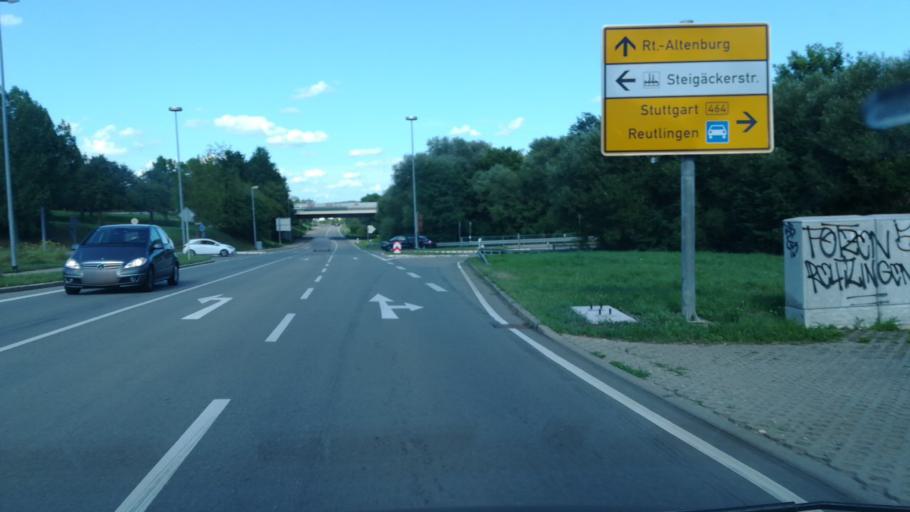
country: DE
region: Baden-Wuerttemberg
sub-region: Tuebingen Region
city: Sickenhausen
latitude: 48.5433
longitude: 9.1756
